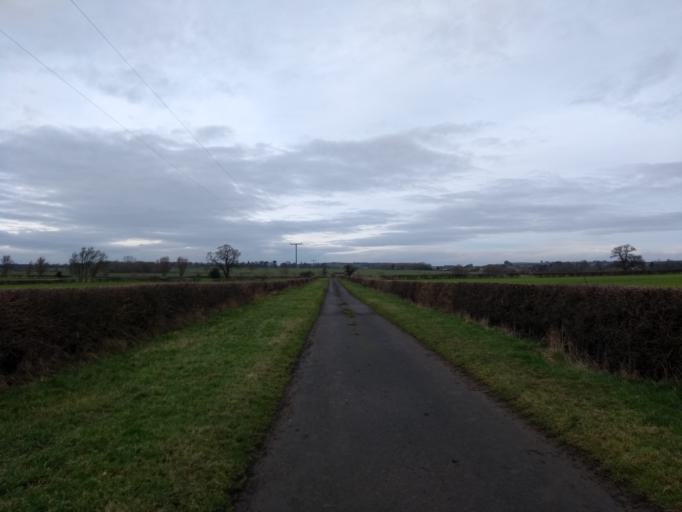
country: GB
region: England
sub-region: East Riding of Yorkshire
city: Stamford Bridge
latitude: 54.0649
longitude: -0.9307
